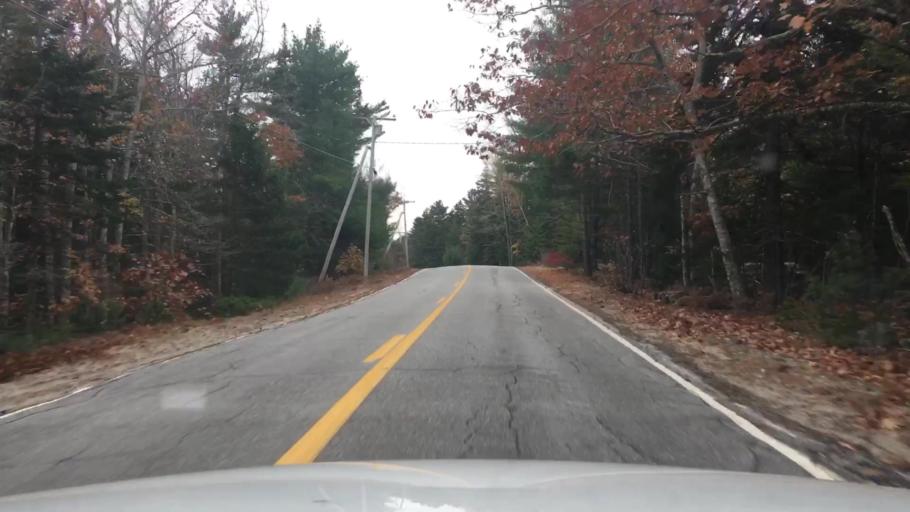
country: US
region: Maine
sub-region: Hancock County
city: Sedgwick
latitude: 44.3351
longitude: -68.5658
